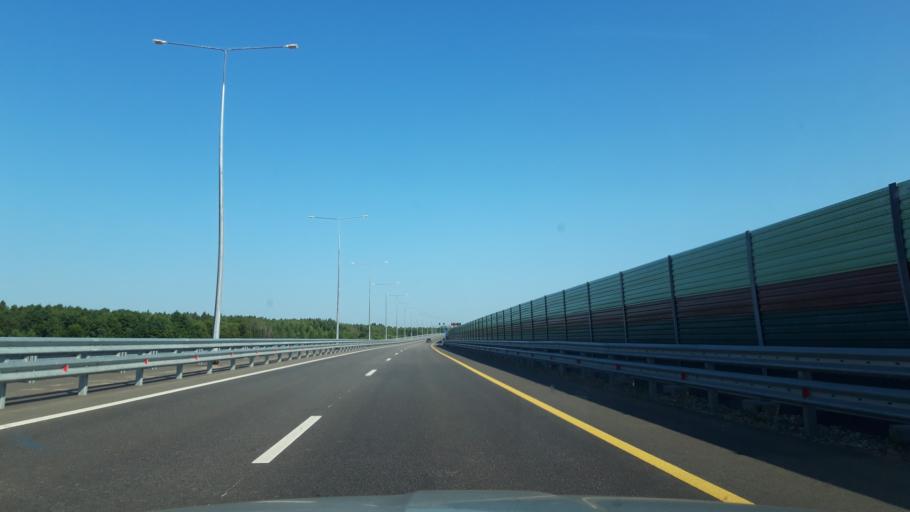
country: RU
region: Tverskaya
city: Zavidovo
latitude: 56.5137
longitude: 36.5082
